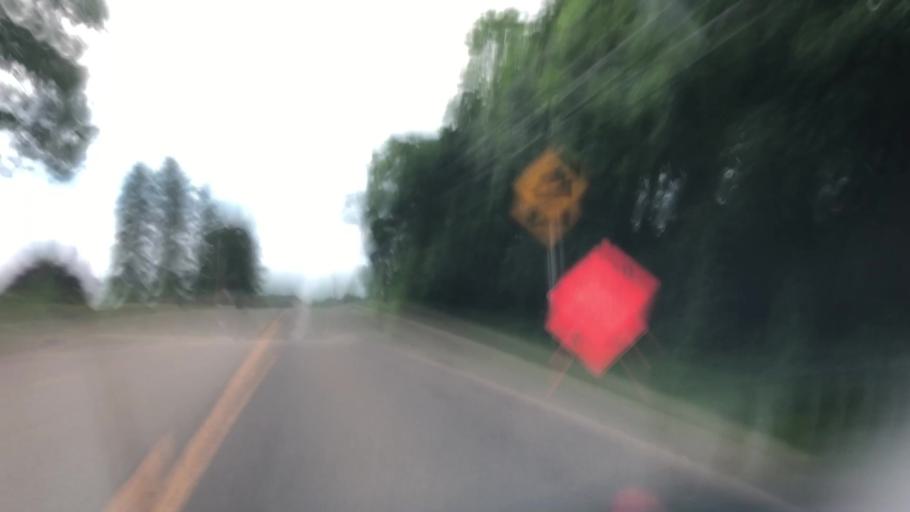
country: US
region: Ohio
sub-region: Stark County
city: Perry Heights
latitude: 40.8085
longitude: -81.4838
